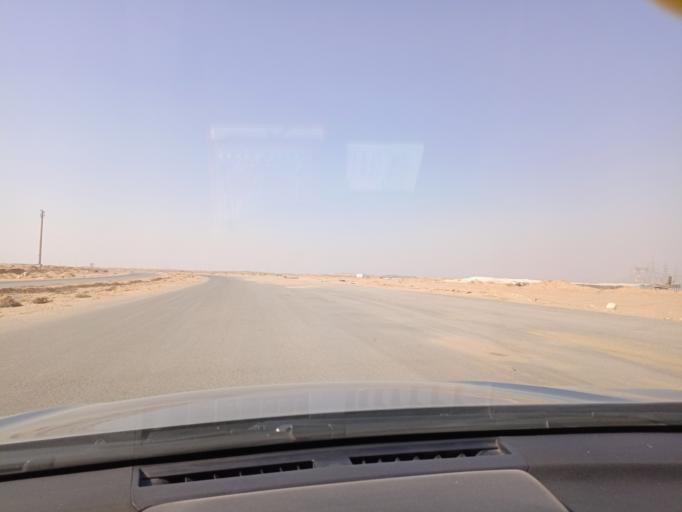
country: EG
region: Muhafazat al Qalyubiyah
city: Al Khankah
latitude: 30.0386
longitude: 31.7163
